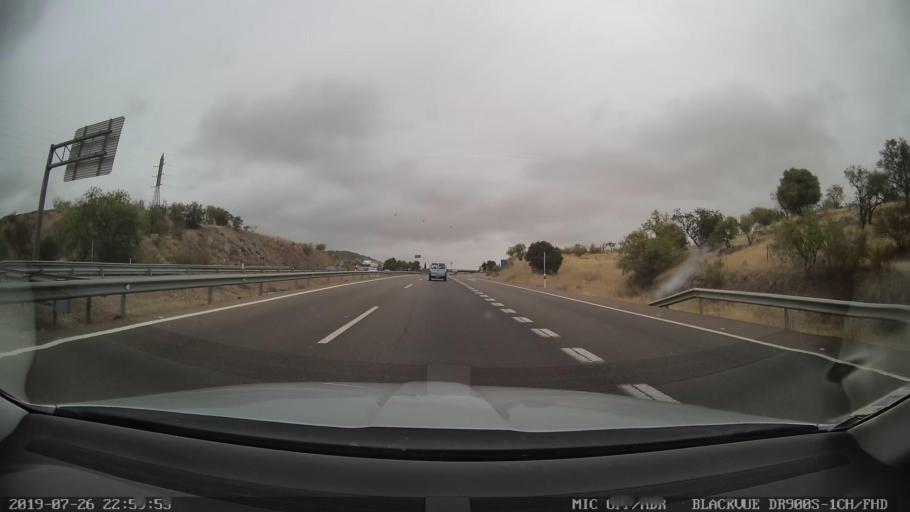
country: ES
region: Extremadura
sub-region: Provincia de Badajoz
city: Merida
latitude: 38.9340
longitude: -6.3658
